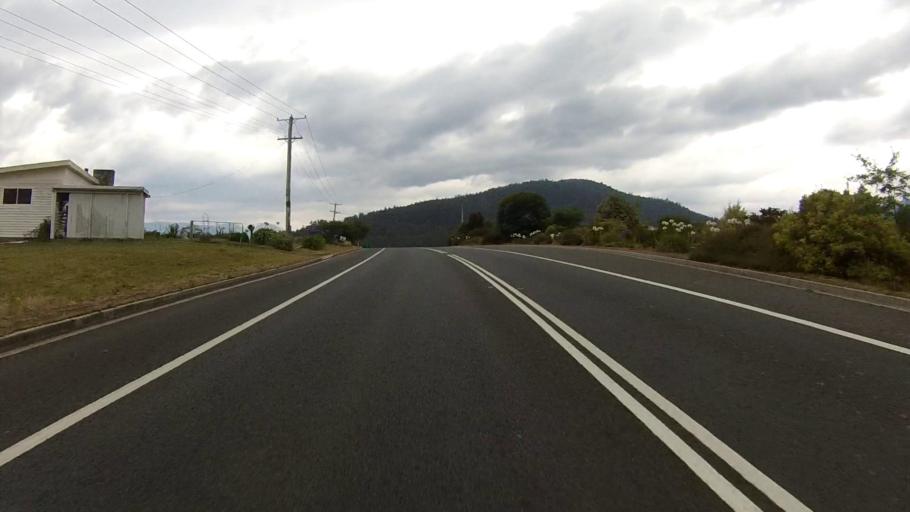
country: AU
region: Tasmania
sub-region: Huon Valley
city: Franklin
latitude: -43.0741
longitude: 147.0361
